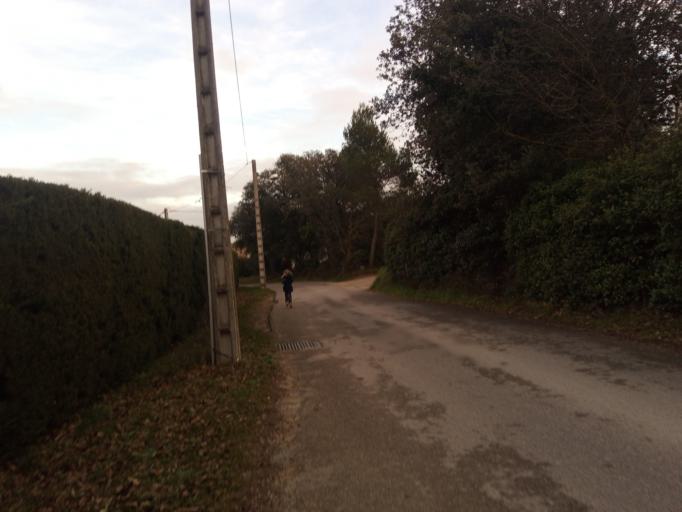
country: FR
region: Provence-Alpes-Cote d'Azur
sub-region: Departement du Vaucluse
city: Lauris
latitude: 43.7477
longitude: 5.3225
